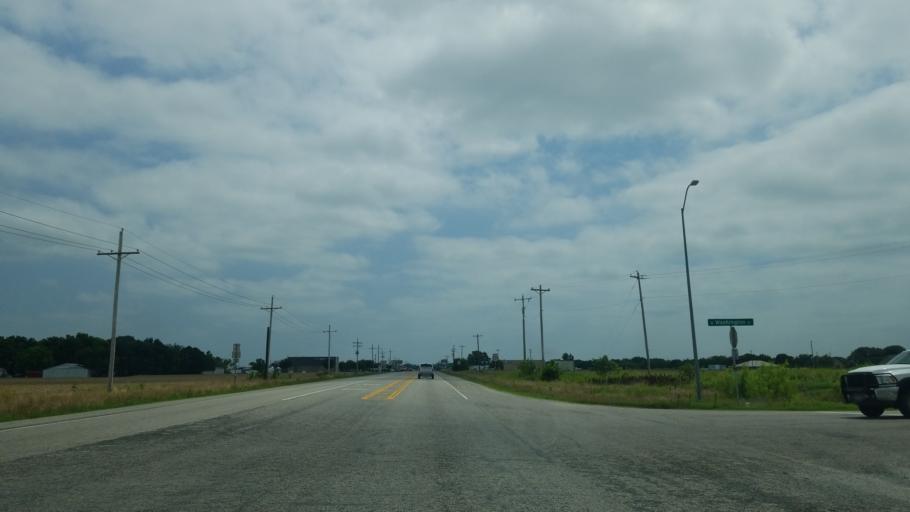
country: US
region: Texas
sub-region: Denton County
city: Pilot Point
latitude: 33.4129
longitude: -96.9407
